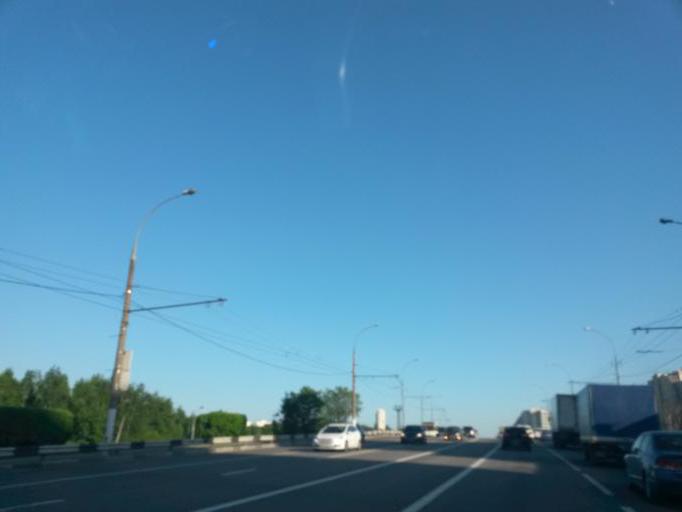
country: RU
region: Moscow
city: Biryulevo
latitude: 55.5905
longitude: 37.6738
